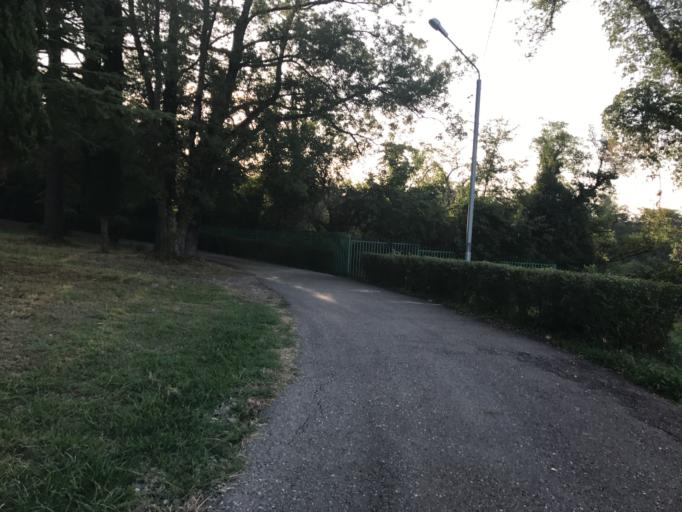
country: RU
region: Krasnodarskiy
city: Shepsi
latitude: 44.0063
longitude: 39.1813
